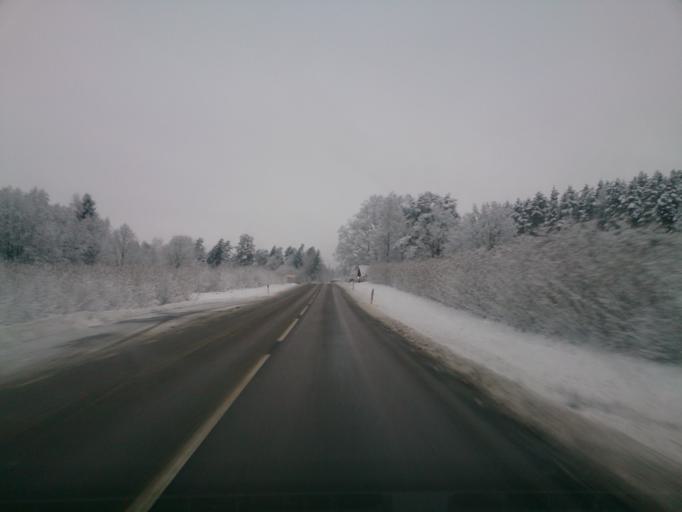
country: SE
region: OEstergoetland
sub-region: Atvidabergs Kommun
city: Atvidaberg
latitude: 58.3032
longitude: 15.8873
